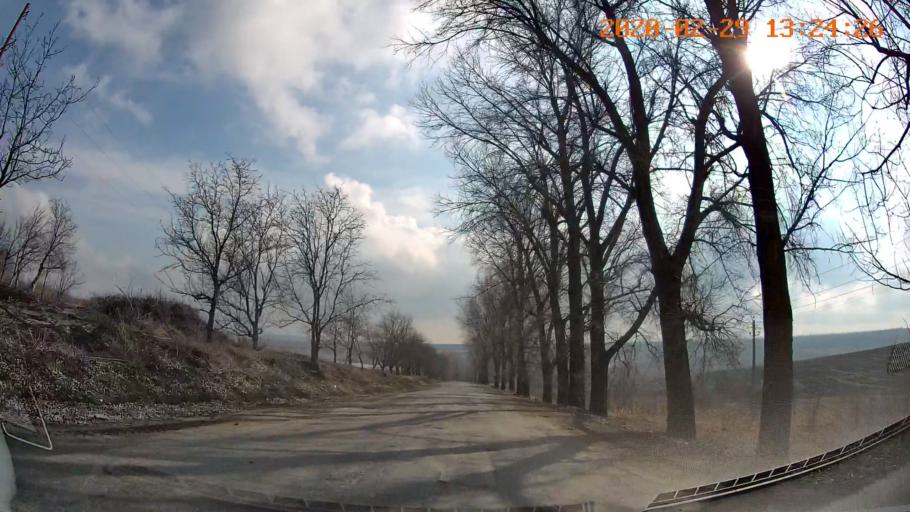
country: MD
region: Telenesti
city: Camenca
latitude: 47.9388
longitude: 28.6275
